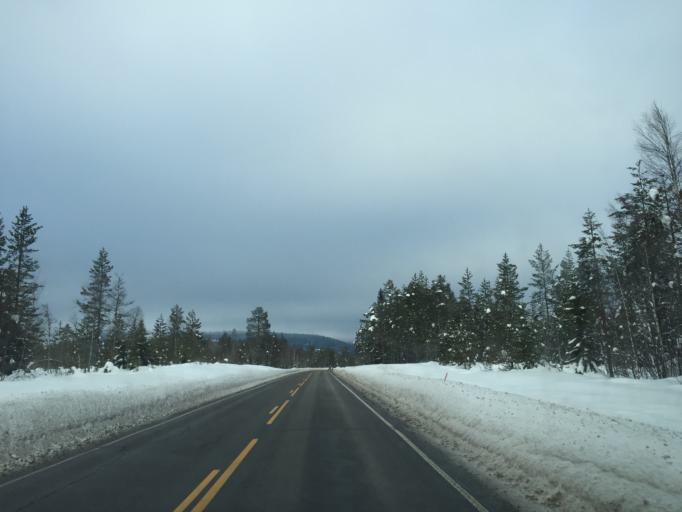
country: NO
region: Hedmark
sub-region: Trysil
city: Innbygda
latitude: 61.1523
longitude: 12.1324
